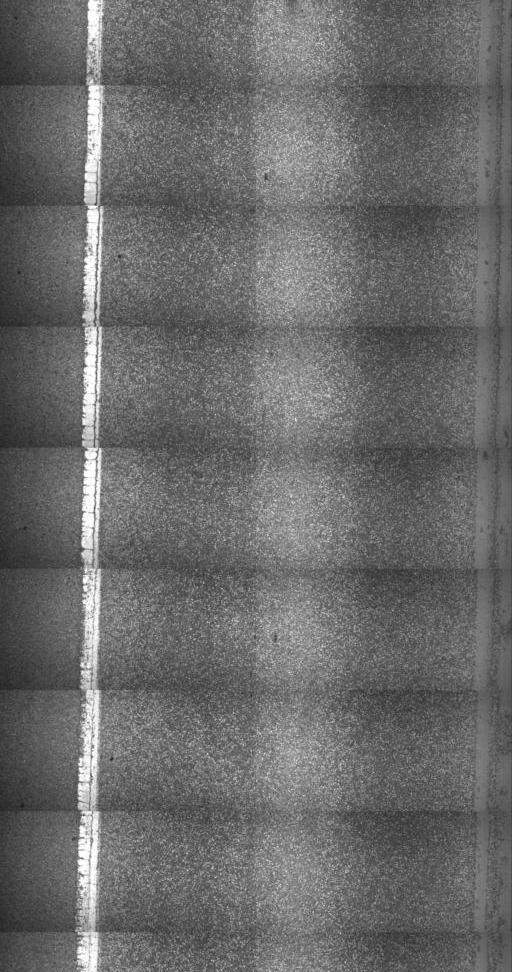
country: US
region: Vermont
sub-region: Washington County
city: Waterbury
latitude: 44.2575
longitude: -72.7543
